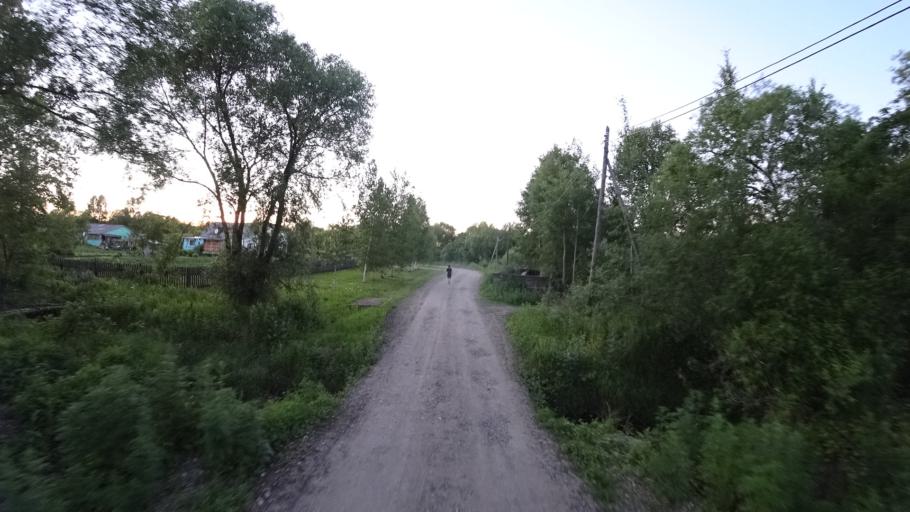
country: RU
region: Khabarovsk Krai
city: Khor
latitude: 47.8490
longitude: 134.9537
